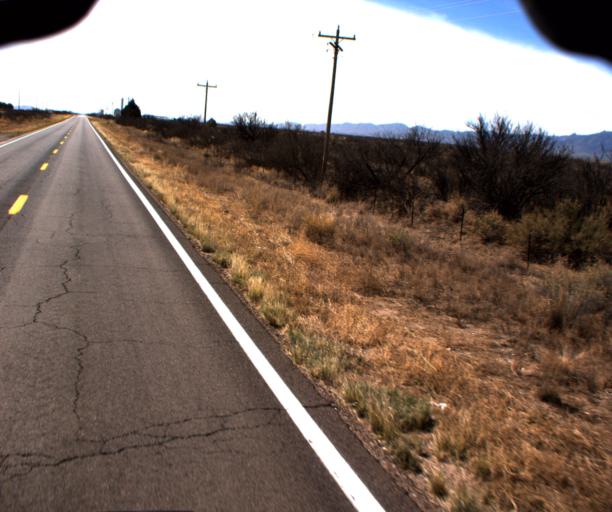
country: US
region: Arizona
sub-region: Cochise County
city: Willcox
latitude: 32.0957
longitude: -109.9091
